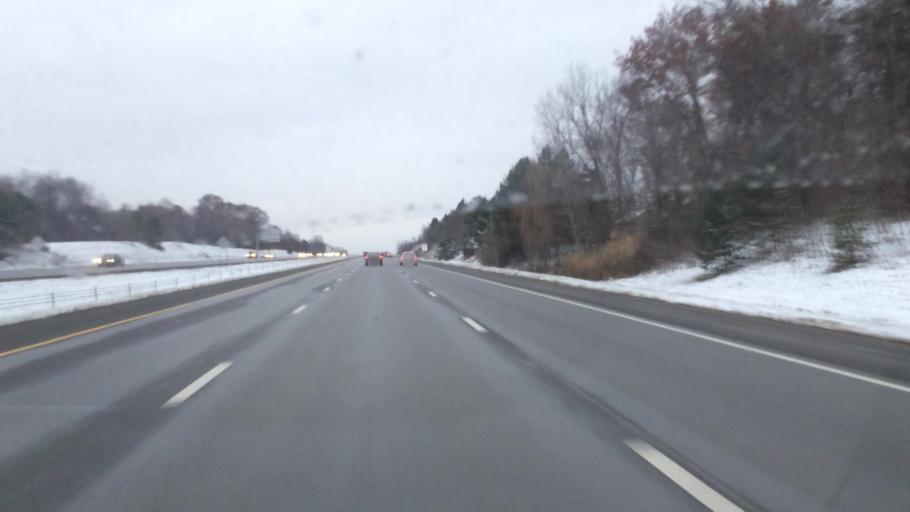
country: US
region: Ohio
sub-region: Medina County
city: Brunswick
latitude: 41.1784
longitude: -81.7879
